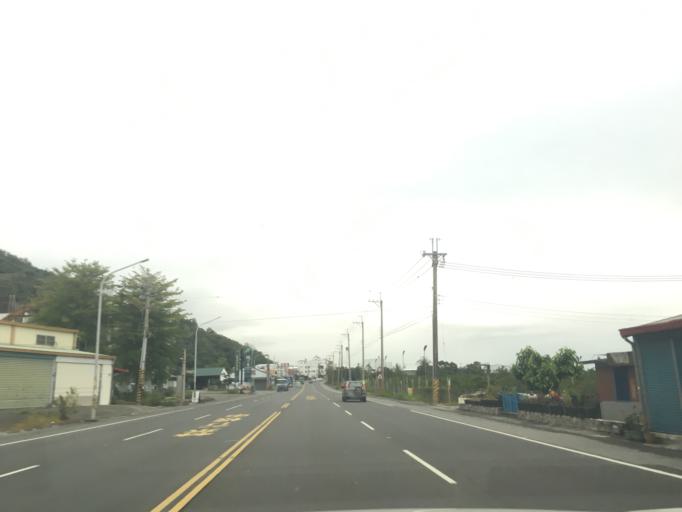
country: TW
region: Taiwan
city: Taitung City
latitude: 22.6809
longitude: 121.0424
